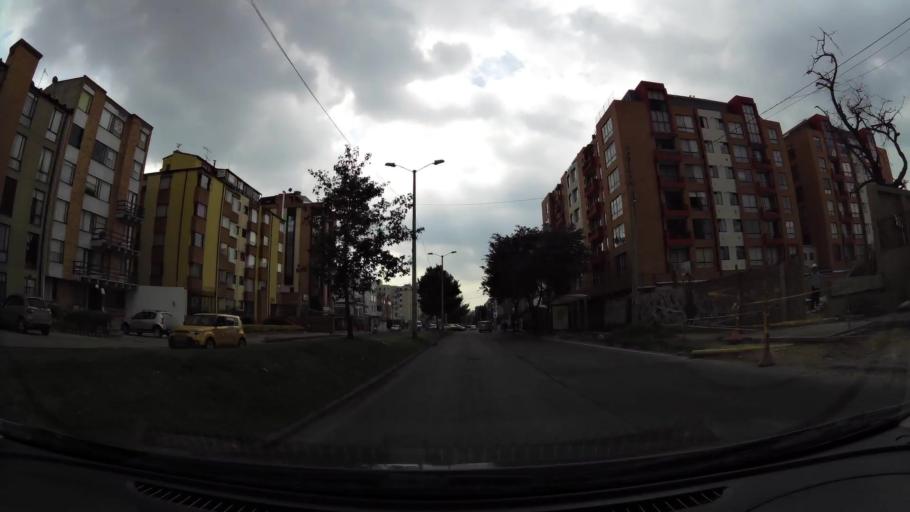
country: CO
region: Bogota D.C.
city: Barrio San Luis
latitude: 4.7274
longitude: -74.0367
